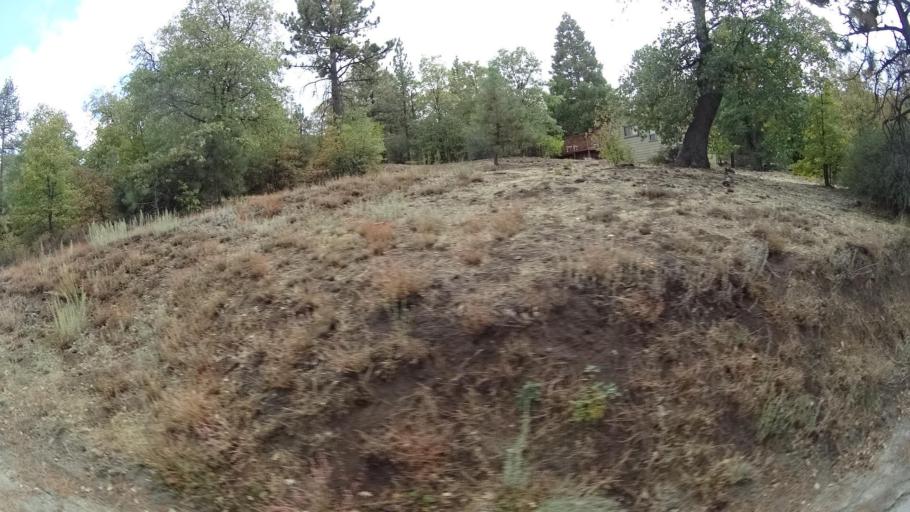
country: US
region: California
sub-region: San Diego County
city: Pine Valley
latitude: 32.8687
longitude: -116.4215
